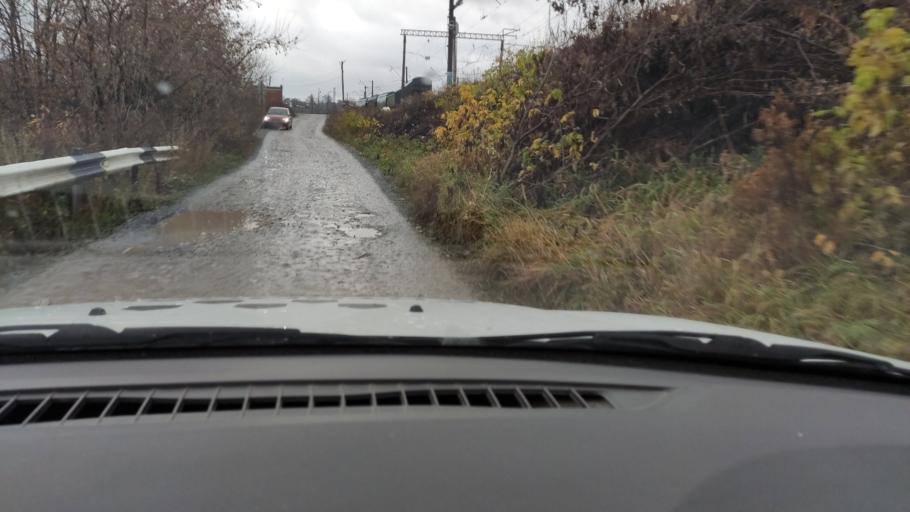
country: RU
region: Perm
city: Sylva
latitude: 58.0431
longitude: 56.7468
